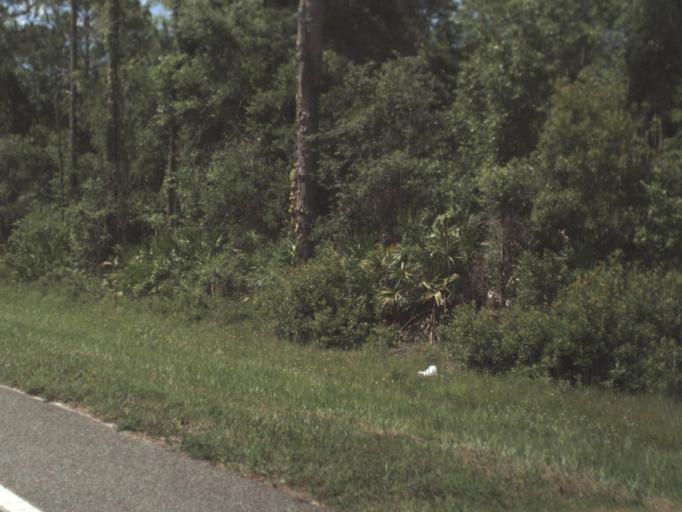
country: US
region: Florida
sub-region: Putnam County
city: East Palatka
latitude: 29.5832
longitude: -81.5604
